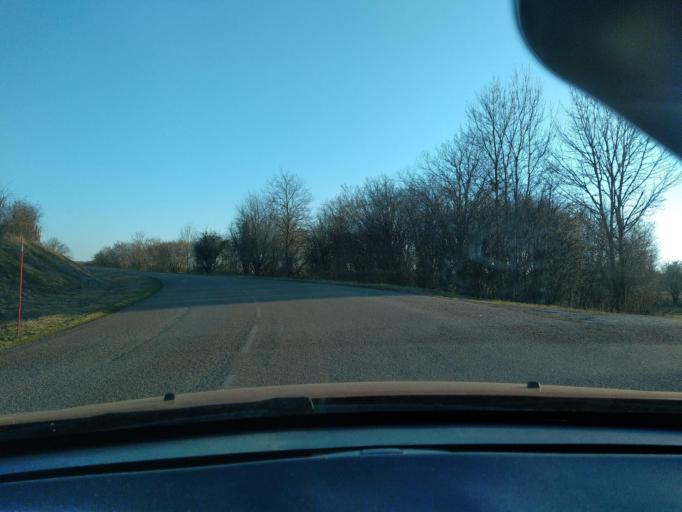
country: FR
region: Franche-Comte
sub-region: Departement du Jura
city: Perrigny
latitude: 46.6457
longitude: 5.6426
